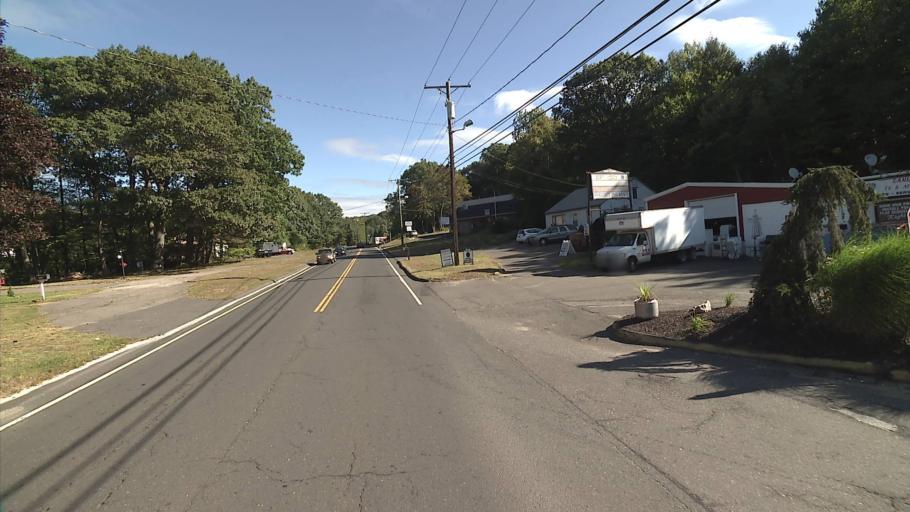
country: US
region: Connecticut
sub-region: New Haven County
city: Wolcott
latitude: 41.5959
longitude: -72.9866
